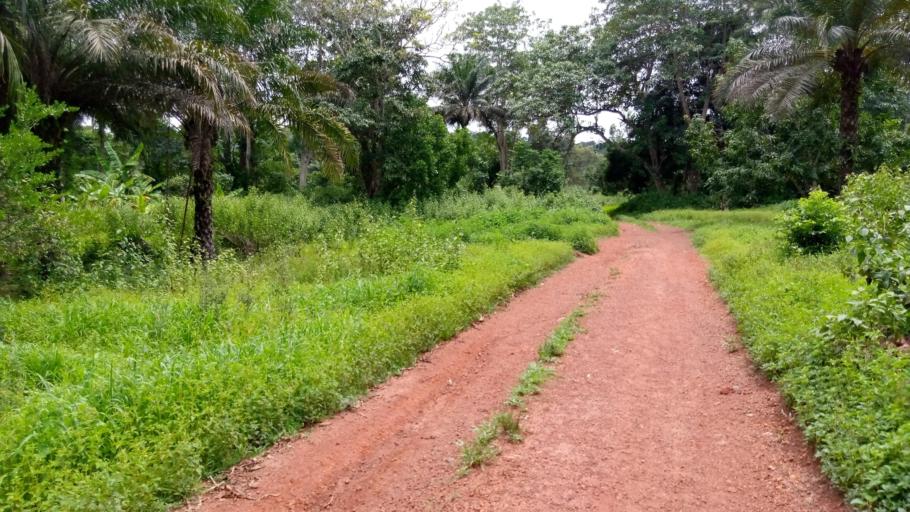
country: SL
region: Southern Province
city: Rotifunk
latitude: 8.1938
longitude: -12.5675
